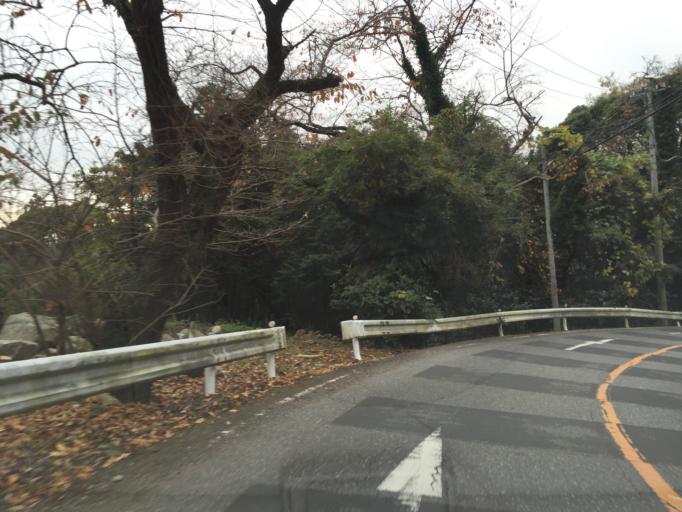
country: JP
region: Ibaraki
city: Tsukuba
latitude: 36.2091
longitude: 140.0860
